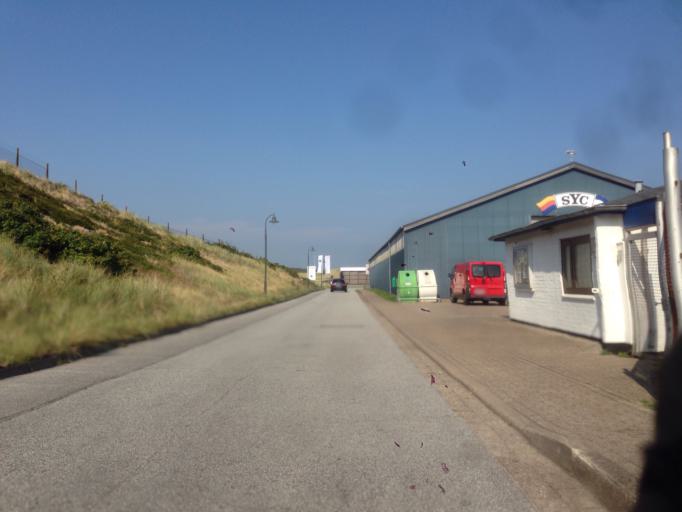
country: DE
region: Schleswig-Holstein
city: Norddorf
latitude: 54.7598
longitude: 8.2947
